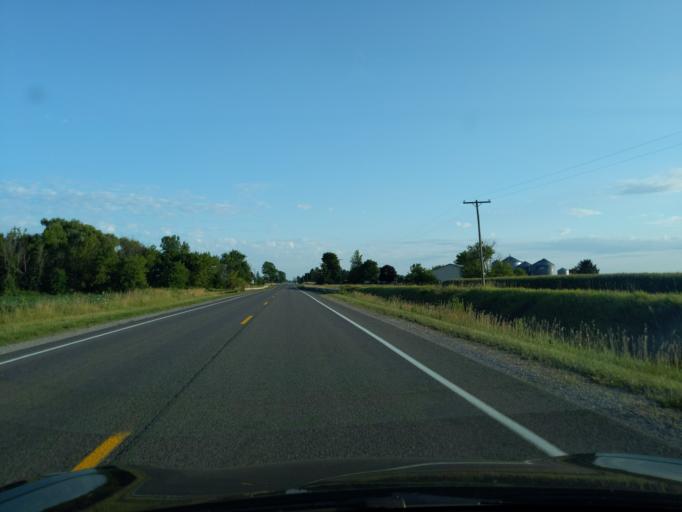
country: US
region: Michigan
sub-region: Gratiot County
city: Breckenridge
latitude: 43.5091
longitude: -84.3698
